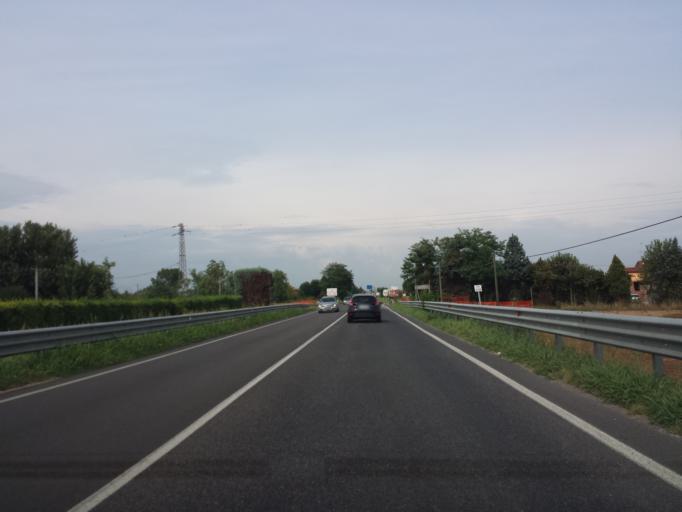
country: IT
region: Veneto
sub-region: Provincia di Vicenza
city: Brendola
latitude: 45.4815
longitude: 11.4184
